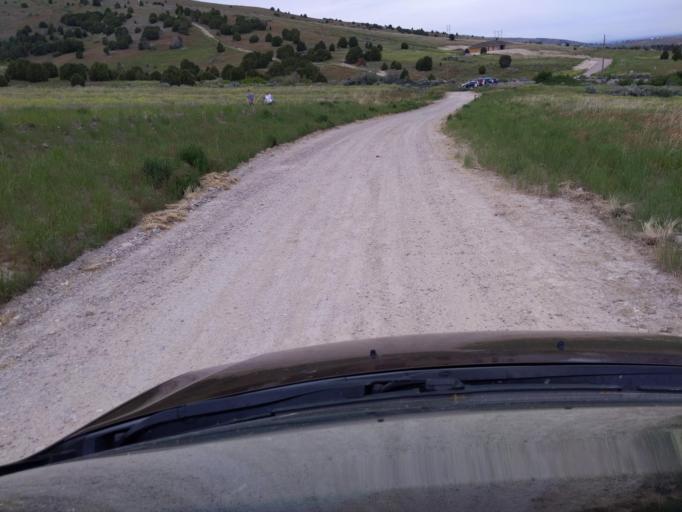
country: US
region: Idaho
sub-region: Bannock County
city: Pocatello
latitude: 42.8467
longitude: -112.4594
